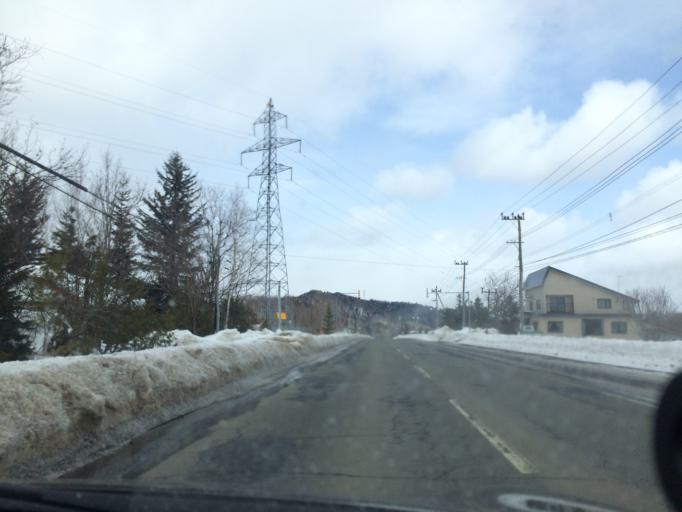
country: JP
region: Hokkaido
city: Shimo-furano
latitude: 42.9961
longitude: 142.4032
